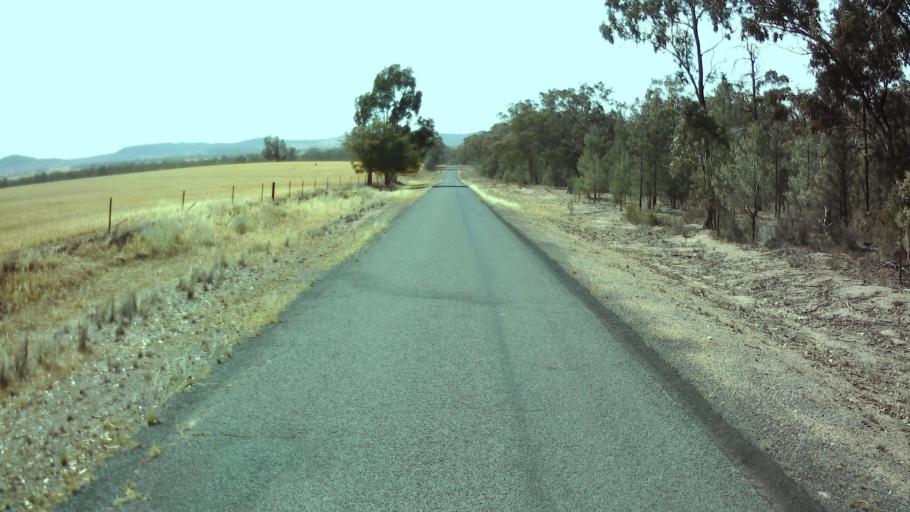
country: AU
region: New South Wales
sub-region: Weddin
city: Grenfell
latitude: -33.7528
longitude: 148.0699
